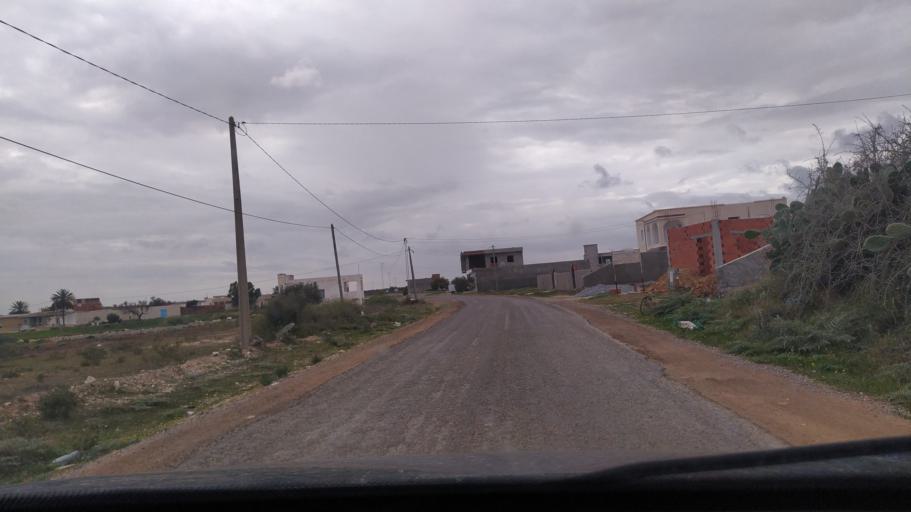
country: TN
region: Al Munastir
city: Sidi Bin Nur
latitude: 35.5093
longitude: 10.9631
